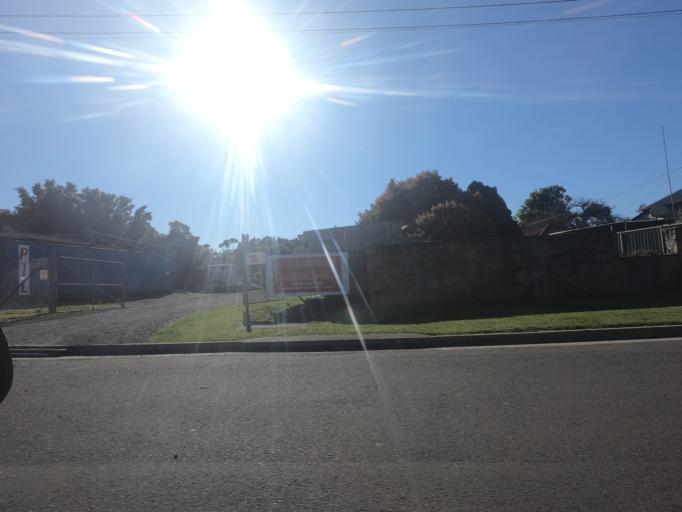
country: AU
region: New South Wales
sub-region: Wollongong
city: Corrimal
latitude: -34.3744
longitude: 150.8878
